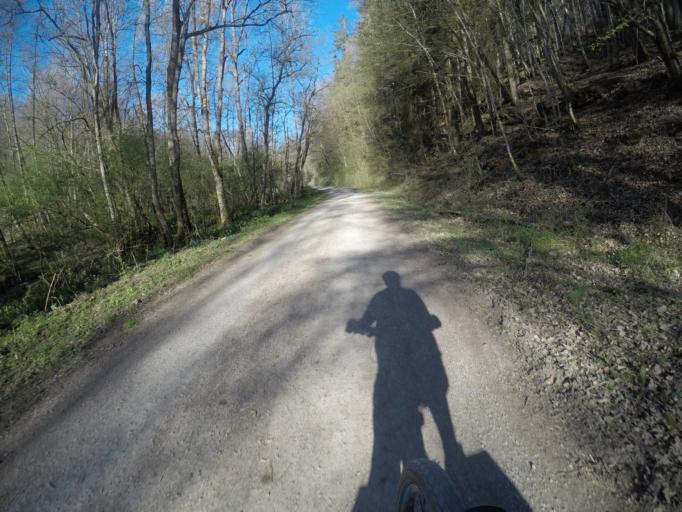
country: DE
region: Baden-Wuerttemberg
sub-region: Regierungsbezirk Stuttgart
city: Waldenbuch
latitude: 48.6054
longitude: 9.1617
